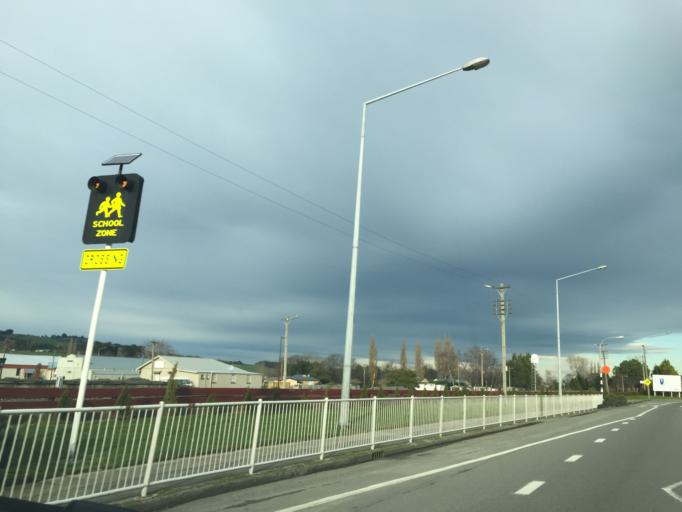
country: NZ
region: Southland
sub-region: Gore District
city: Gore
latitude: -46.1941
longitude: 168.8652
